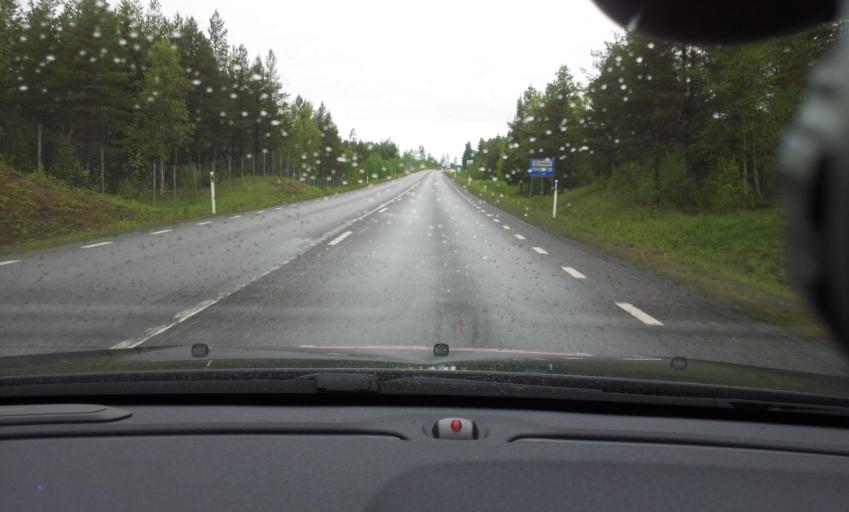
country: SE
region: Jaemtland
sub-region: Krokoms Kommun
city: Valla
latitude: 63.3078
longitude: 13.9168
